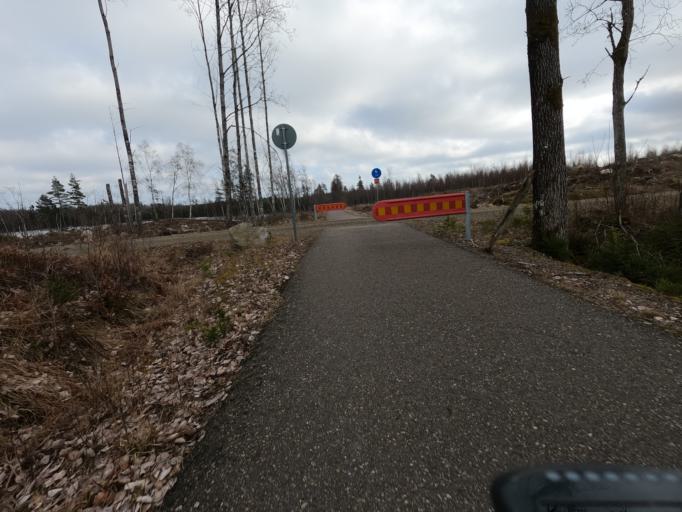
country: SE
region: Joenkoeping
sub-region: Varnamo Kommun
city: Rydaholm
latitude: 56.8436
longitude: 14.2232
